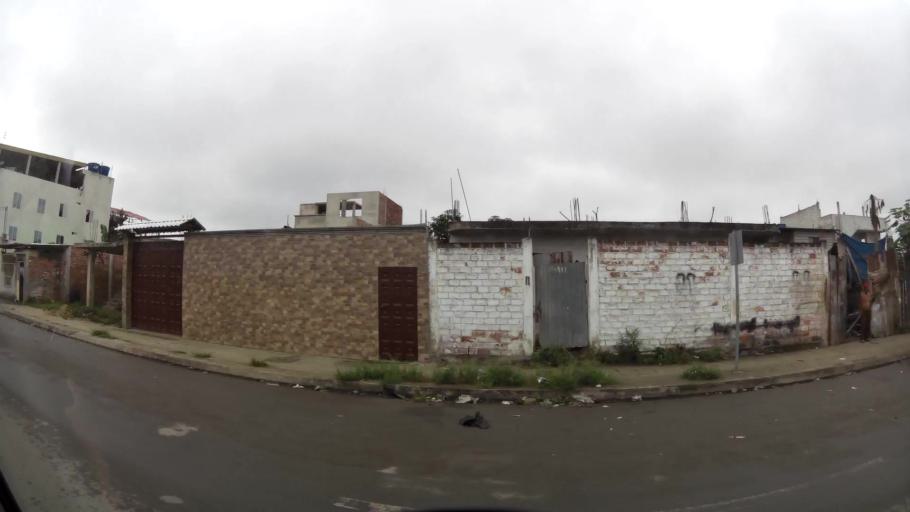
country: EC
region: El Oro
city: Pasaje
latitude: -3.3239
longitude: -79.8151
